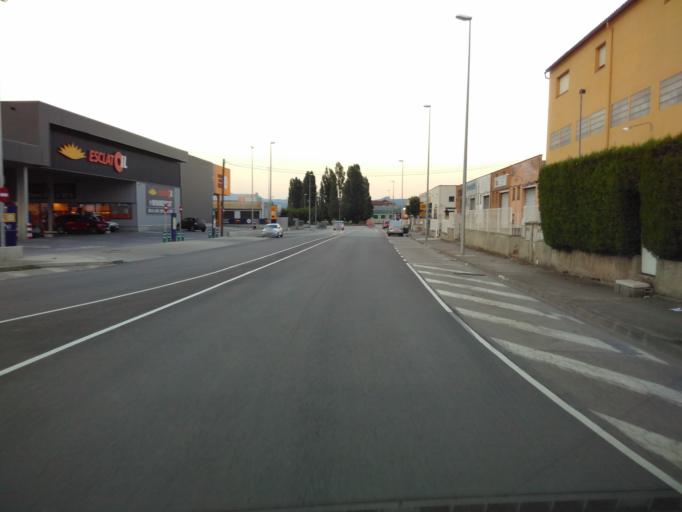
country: ES
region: Catalonia
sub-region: Provincia de Barcelona
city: Vic
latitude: 41.9458
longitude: 2.2531
